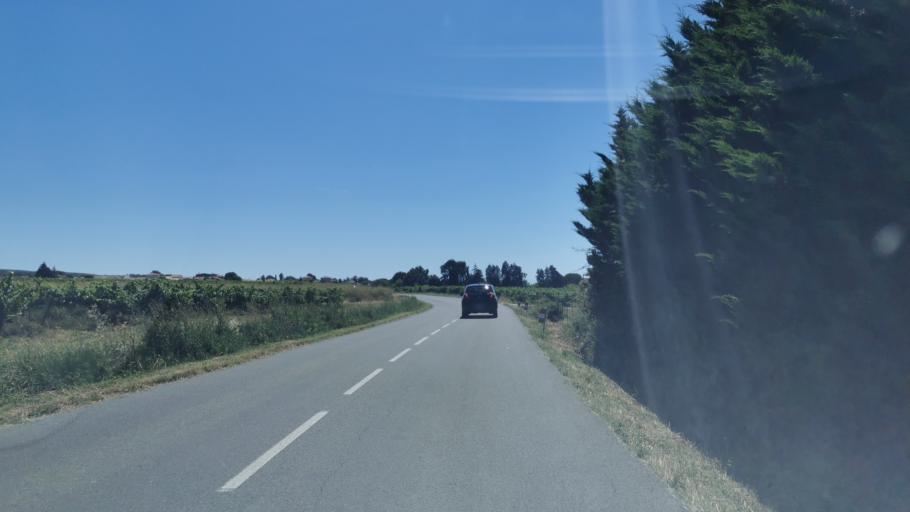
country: FR
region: Languedoc-Roussillon
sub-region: Departement de l'Aude
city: Vinassan
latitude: 43.2138
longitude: 3.0783
